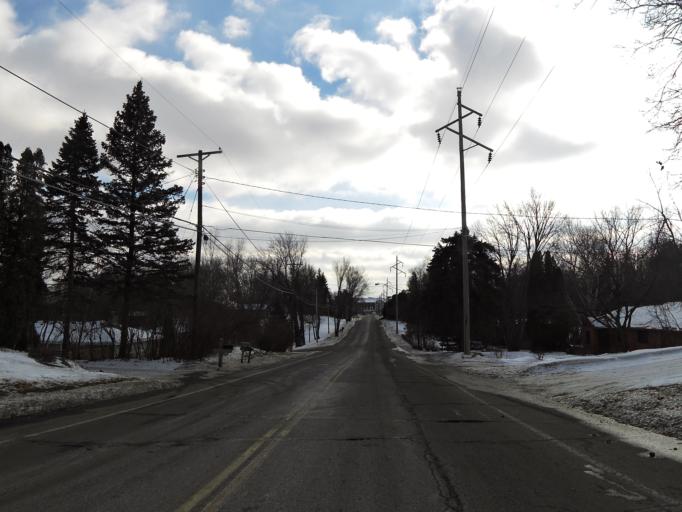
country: US
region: Minnesota
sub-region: Hennepin County
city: Hopkins
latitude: 44.9110
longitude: -93.4628
